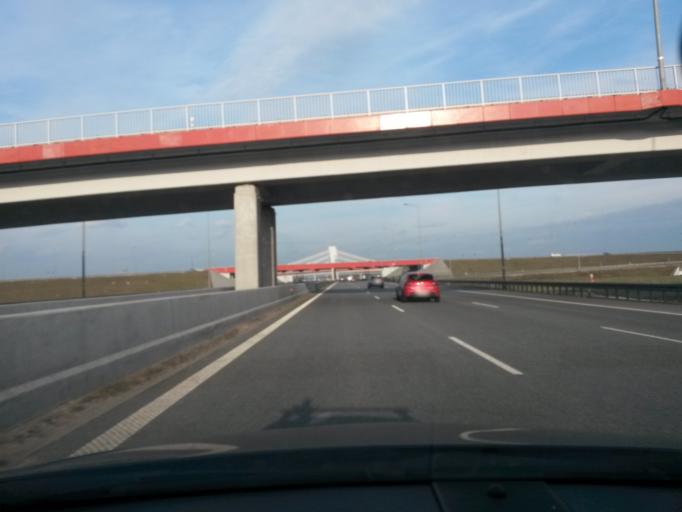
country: PL
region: Lodz Voivodeship
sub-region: Powiat zgierski
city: Strykow
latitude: 51.8913
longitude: 19.6307
